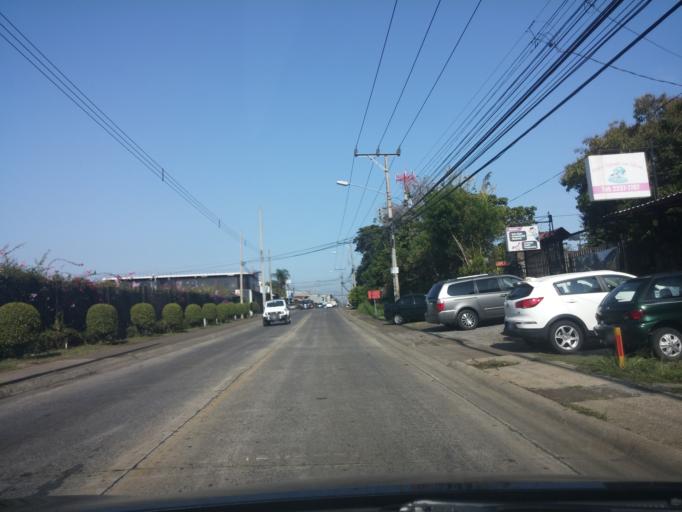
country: CR
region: Heredia
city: San Francisco
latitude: 9.9917
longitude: -84.1355
